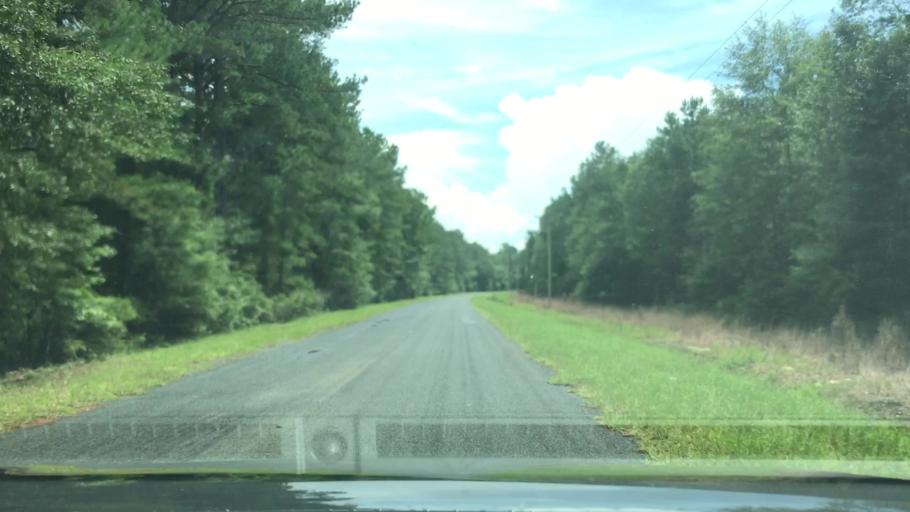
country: US
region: South Carolina
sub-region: Colleton County
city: Walterboro
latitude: 33.0093
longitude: -80.6686
